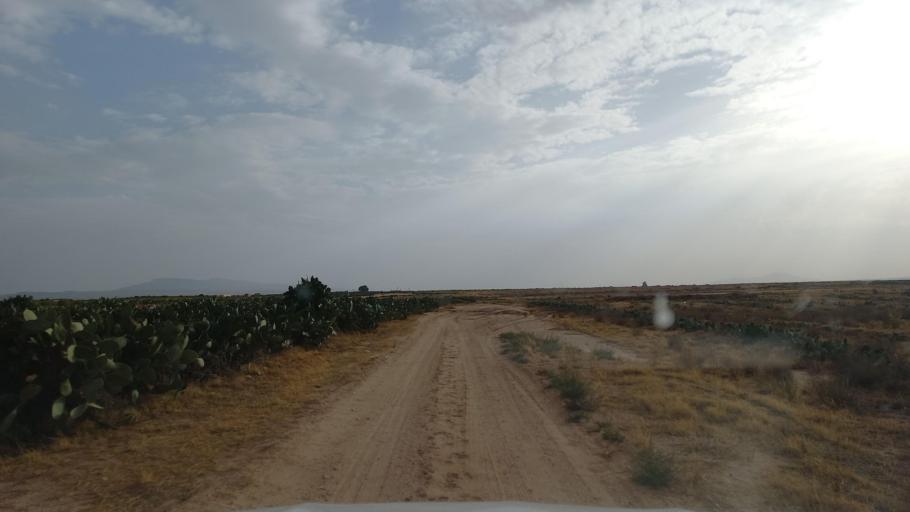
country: TN
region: Al Qasrayn
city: Kasserine
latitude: 35.2916
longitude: 9.0499
